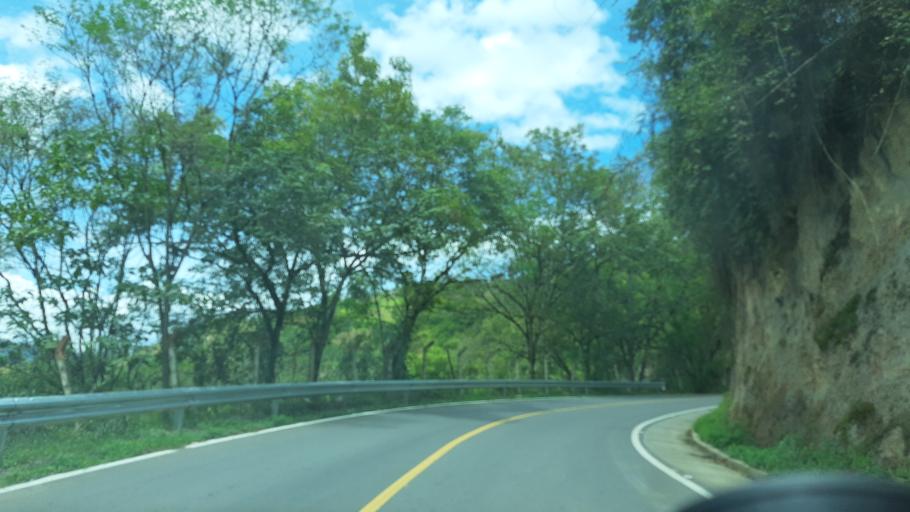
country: CO
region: Boyaca
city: Somondoco
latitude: 5.0079
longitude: -73.4377
